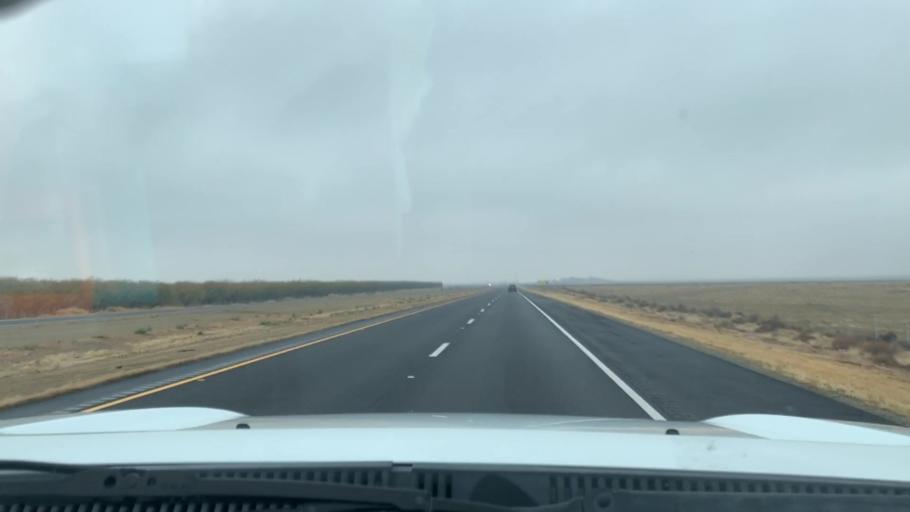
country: US
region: California
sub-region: Kern County
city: Lost Hills
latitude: 35.6146
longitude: -119.8927
